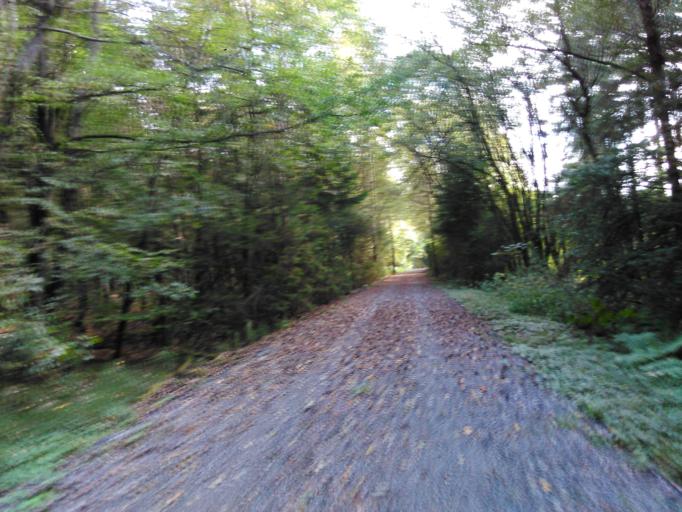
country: BE
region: Wallonia
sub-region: Province du Luxembourg
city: Vaux-sur-Sure
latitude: 49.9364
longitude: 5.5294
